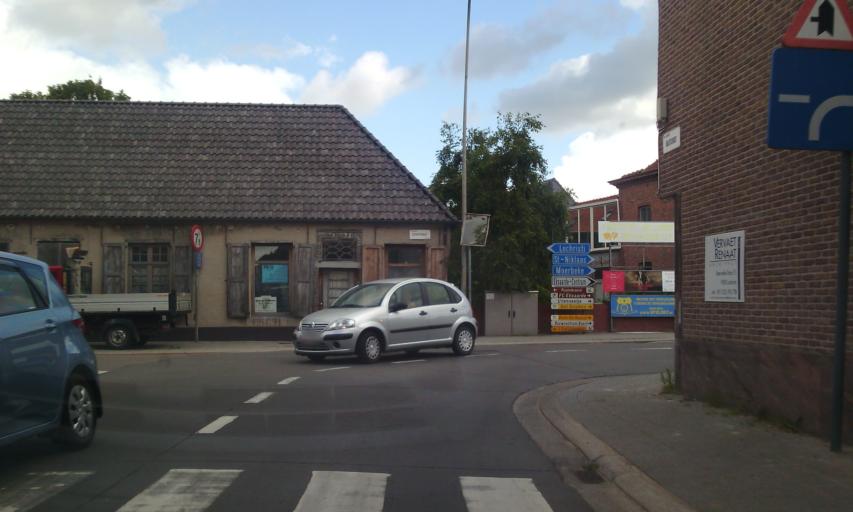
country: BE
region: Flanders
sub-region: Provincie Oost-Vlaanderen
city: Moerbeke
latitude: 51.1458
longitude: 3.9538
